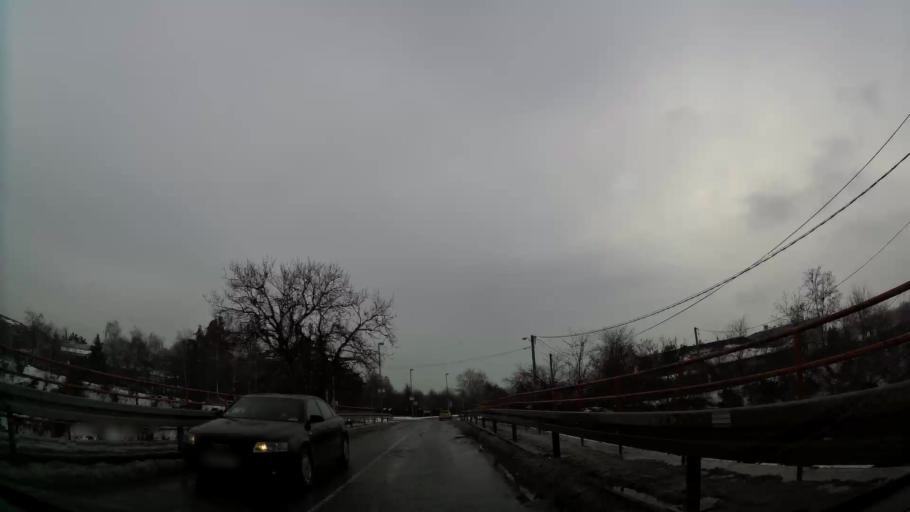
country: RS
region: Central Serbia
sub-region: Belgrade
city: Zemun
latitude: 44.8342
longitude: 20.3907
